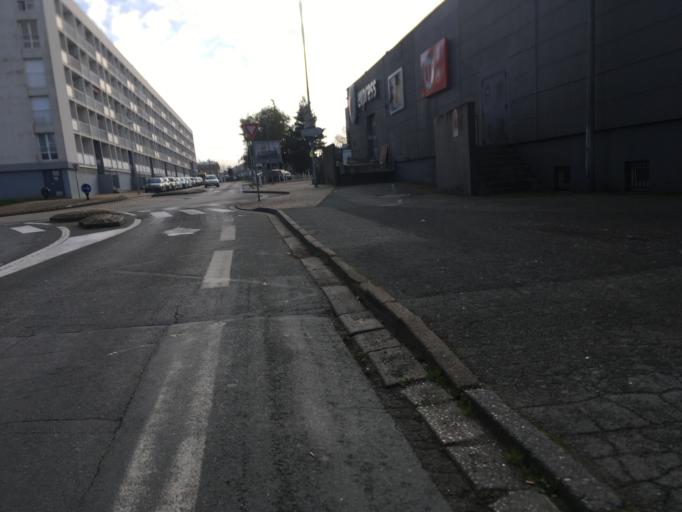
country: FR
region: Poitou-Charentes
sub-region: Departement de la Charente-Maritime
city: La Rochelle
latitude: 46.1675
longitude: -1.1798
